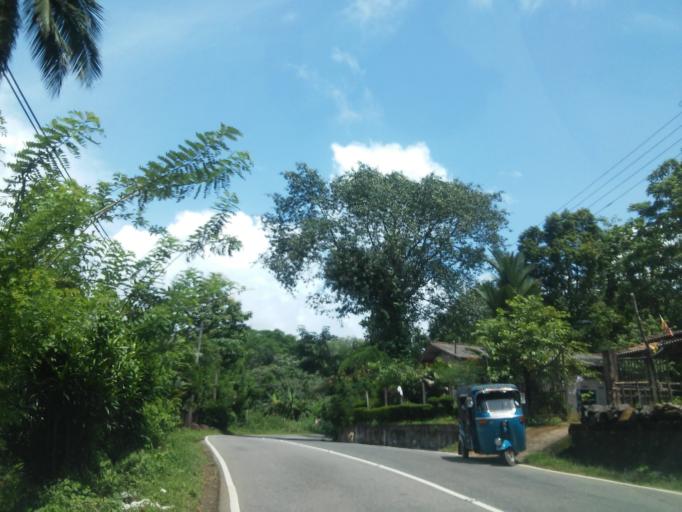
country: LK
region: Sabaragamuwa
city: Ratnapura
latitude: 6.7274
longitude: 80.3218
